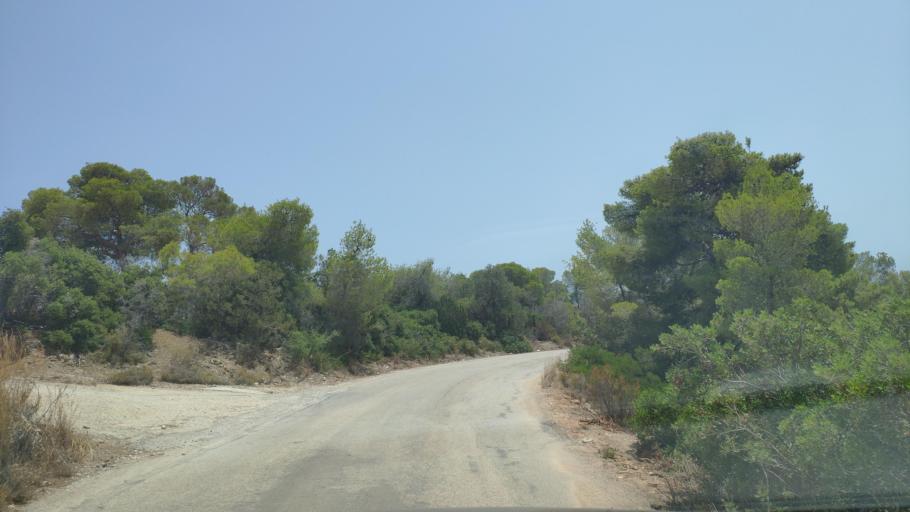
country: GR
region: Peloponnese
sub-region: Nomos Argolidos
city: Porto Cheli
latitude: 37.3080
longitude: 23.1513
